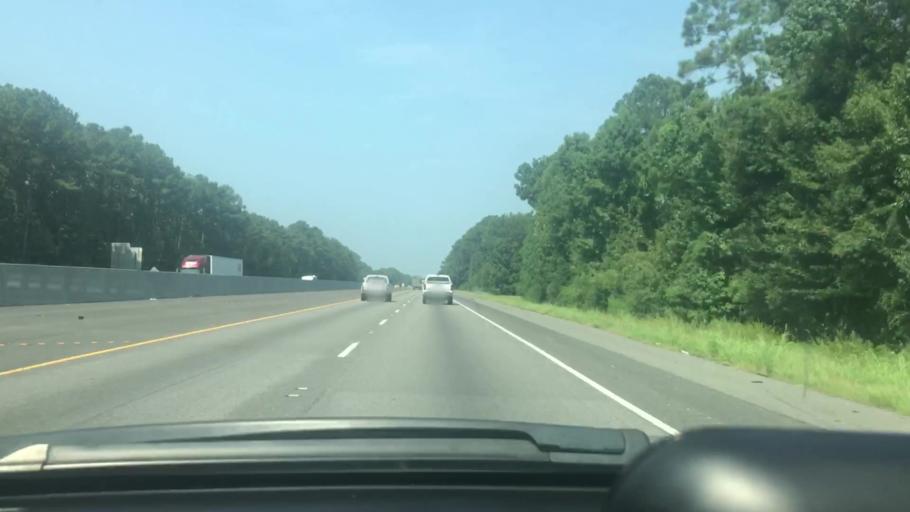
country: US
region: Louisiana
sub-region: Livingston Parish
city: Albany
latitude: 30.4764
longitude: -90.5979
